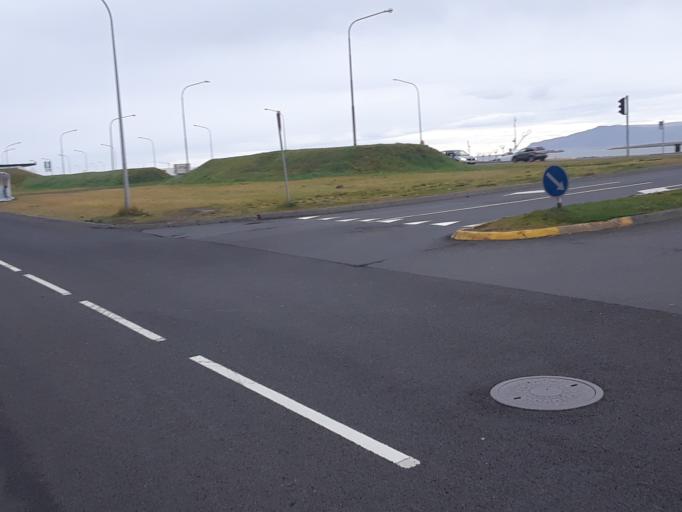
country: IS
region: Capital Region
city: Reykjavik
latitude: 64.1464
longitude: -21.9217
